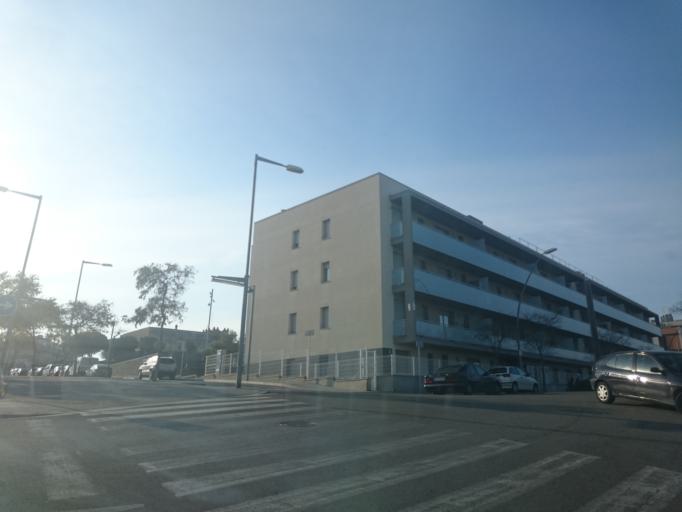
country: ES
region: Catalonia
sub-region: Provincia de Barcelona
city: Vilanova i la Geltru
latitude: 41.2261
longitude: 1.7421
